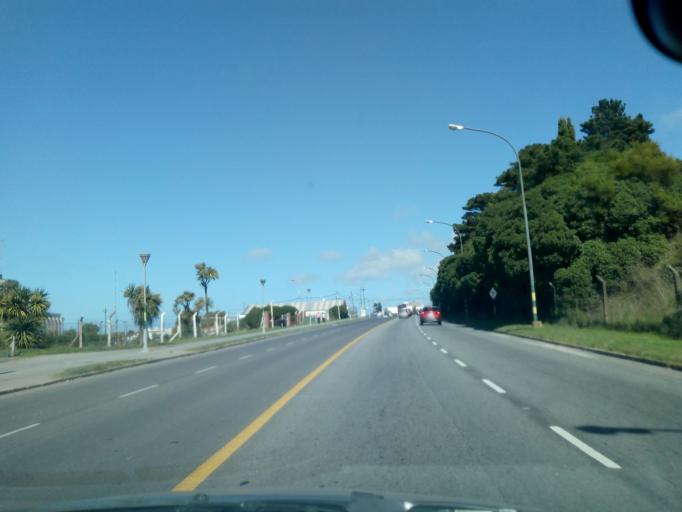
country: AR
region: Buenos Aires
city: Mar del Plata
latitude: -38.0393
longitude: -57.5410
